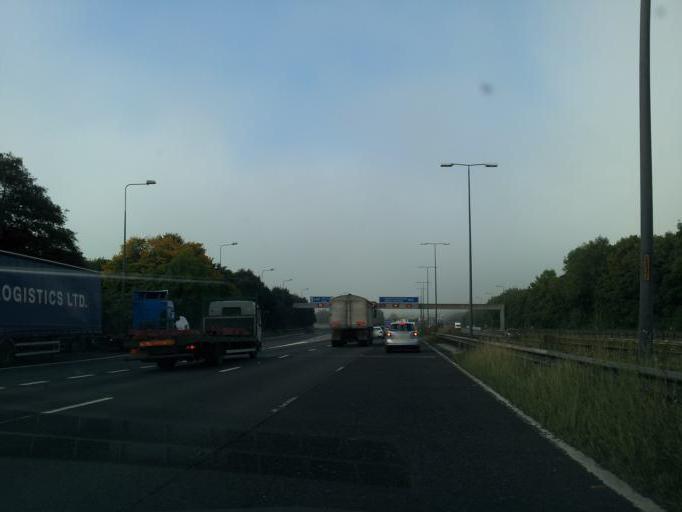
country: GB
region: England
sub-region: Borough of Rochdale
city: Milnrow
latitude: 53.6048
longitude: -2.1031
